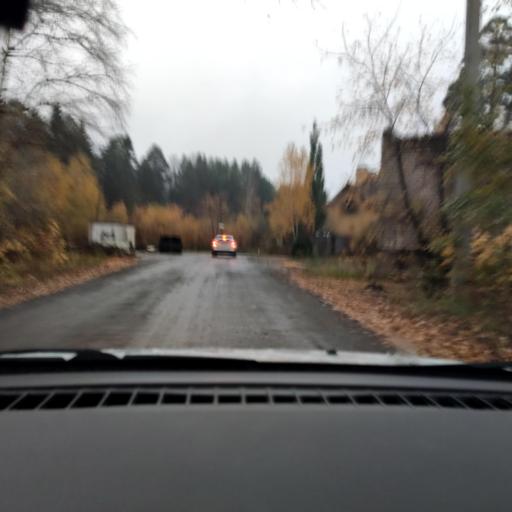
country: RU
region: Perm
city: Kondratovo
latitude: 58.0470
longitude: 56.1044
